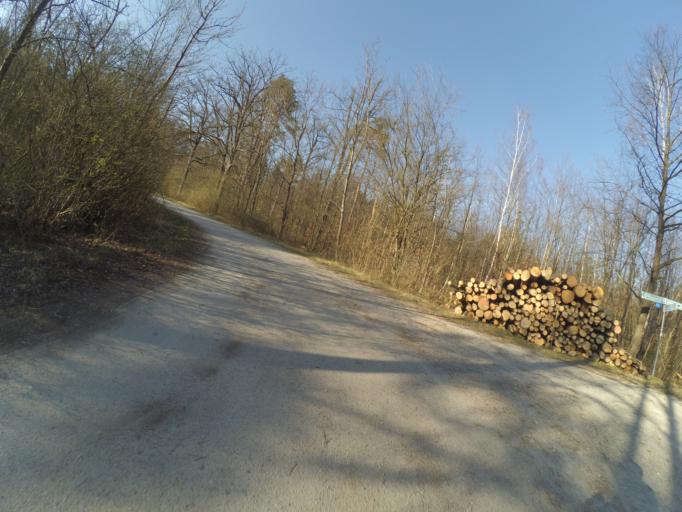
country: DE
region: Bavaria
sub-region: Upper Bavaria
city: Oberschleissheim
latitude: 48.2285
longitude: 11.5611
